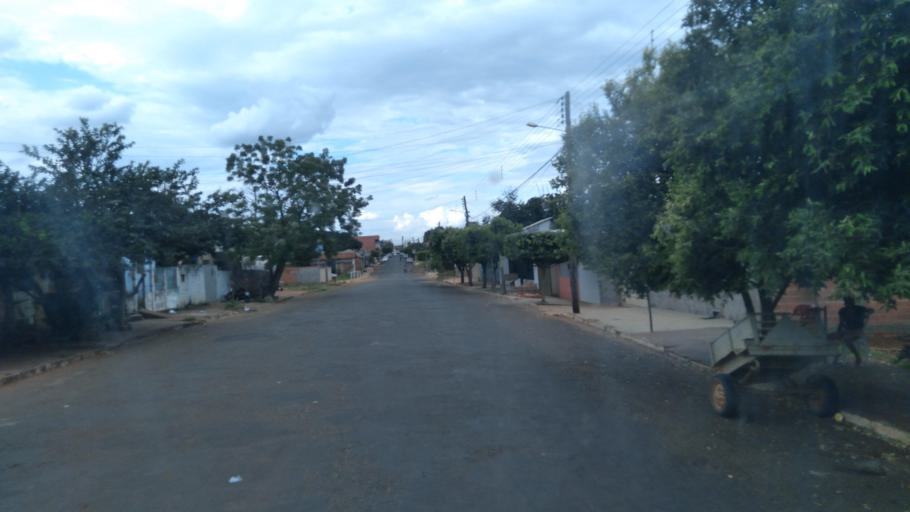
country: BR
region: Goias
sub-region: Mineiros
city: Mineiros
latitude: -17.5726
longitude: -52.5637
